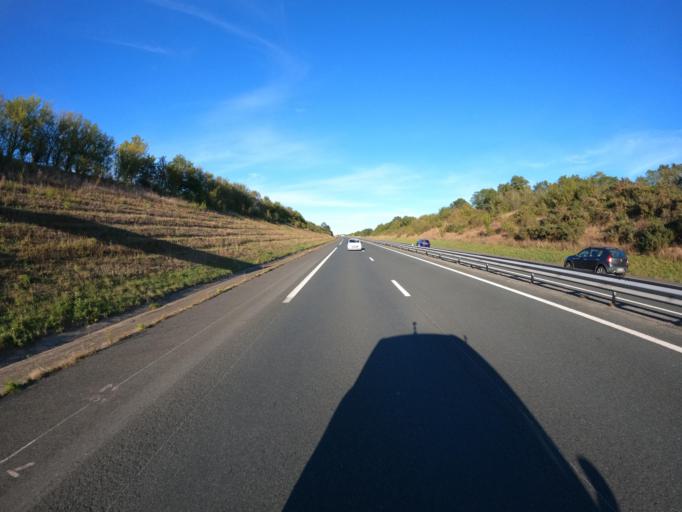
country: FR
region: Pays de la Loire
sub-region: Departement de Maine-et-Loire
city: La Tessoualle
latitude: 47.0349
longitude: -0.8526
